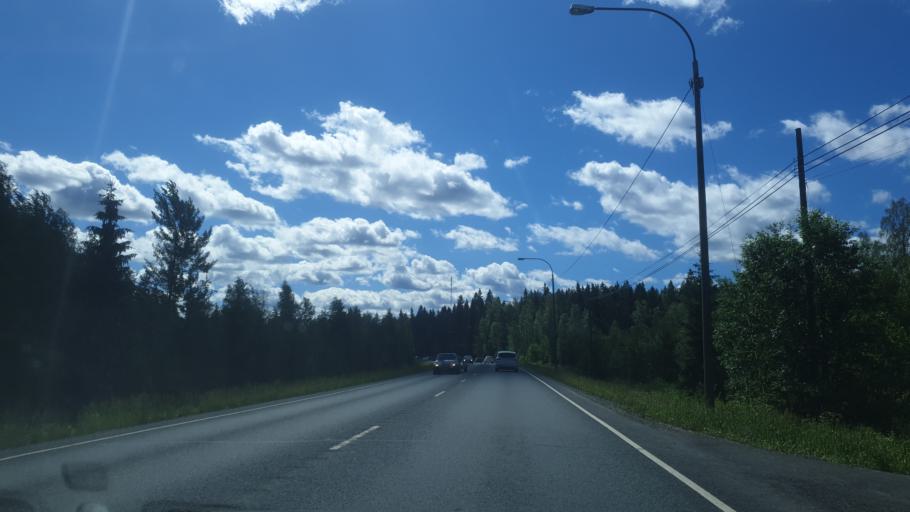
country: FI
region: Northern Savo
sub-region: Varkaus
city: Leppaevirta
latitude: 62.5590
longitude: 27.6203
